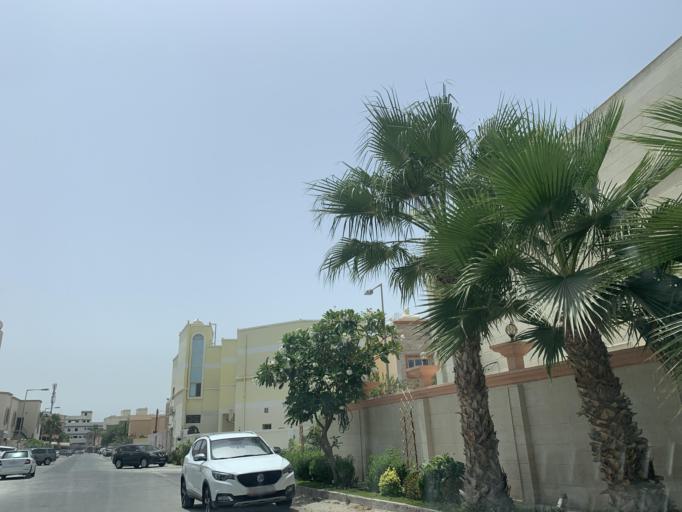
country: BH
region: Northern
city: Sitrah
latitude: 26.1531
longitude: 50.5847
